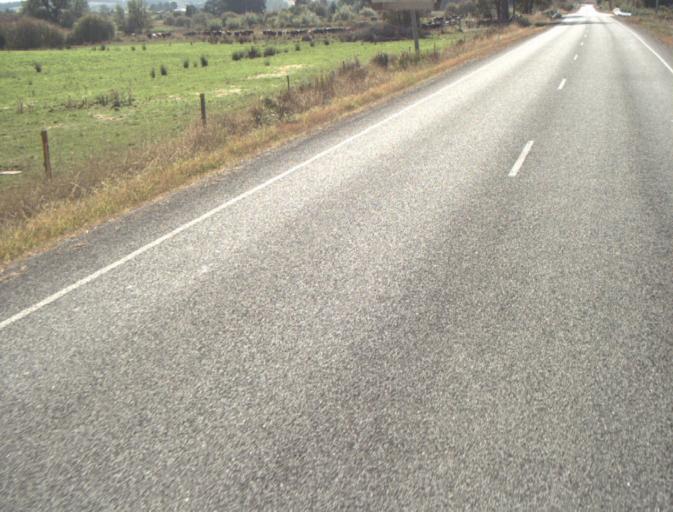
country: AU
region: Tasmania
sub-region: Launceston
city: Mayfield
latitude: -41.2467
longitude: 147.2175
